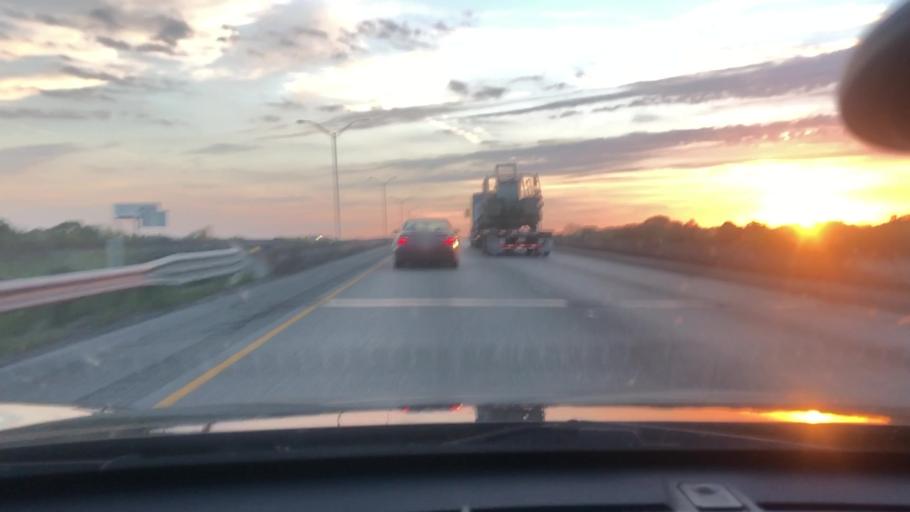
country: US
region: Texas
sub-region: Jackson County
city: Edna
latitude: 28.9869
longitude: -96.6501
